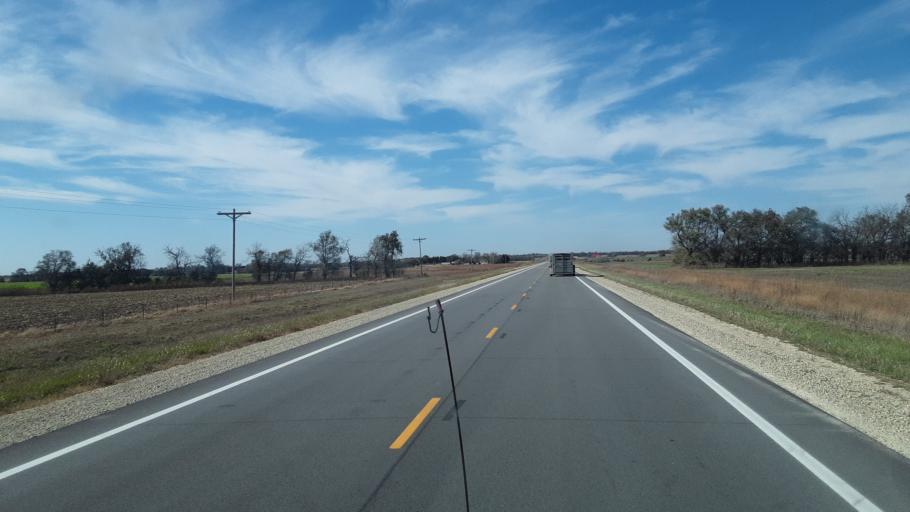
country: US
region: Kansas
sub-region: Marion County
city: Marion
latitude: 38.3629
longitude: -96.9003
